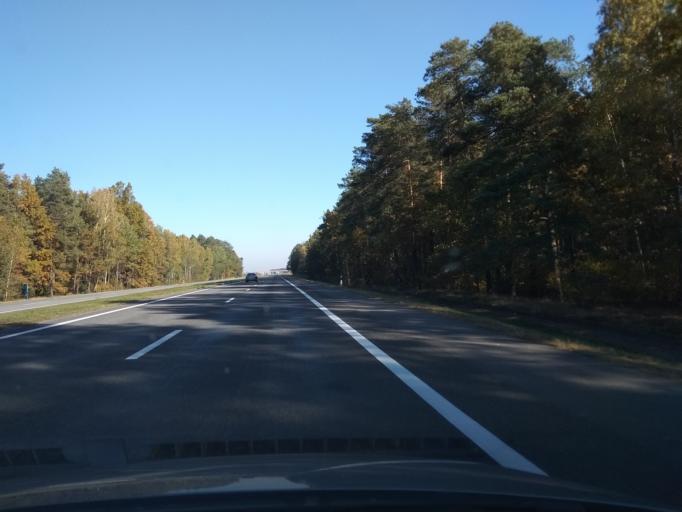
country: BY
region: Brest
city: Antopal'
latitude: 52.3802
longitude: 24.7595
